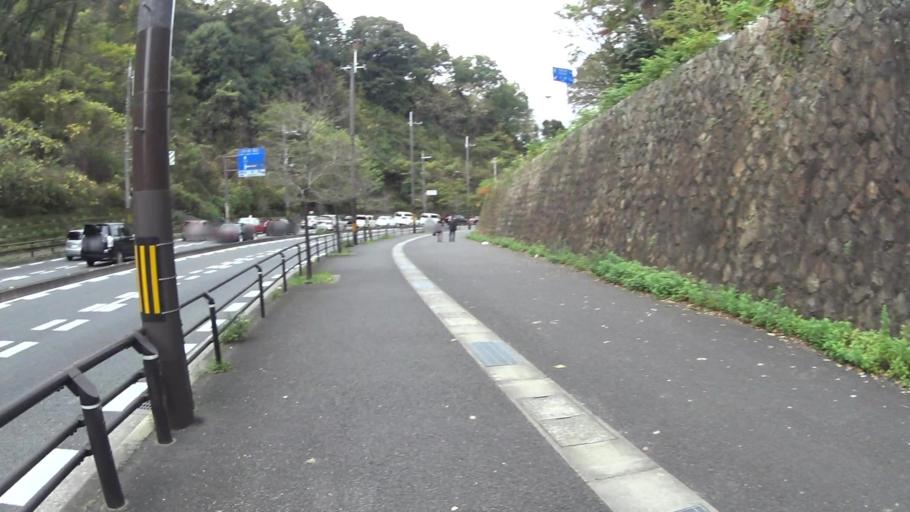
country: JP
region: Kyoto
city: Kyoto
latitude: 35.0037
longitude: 135.7894
